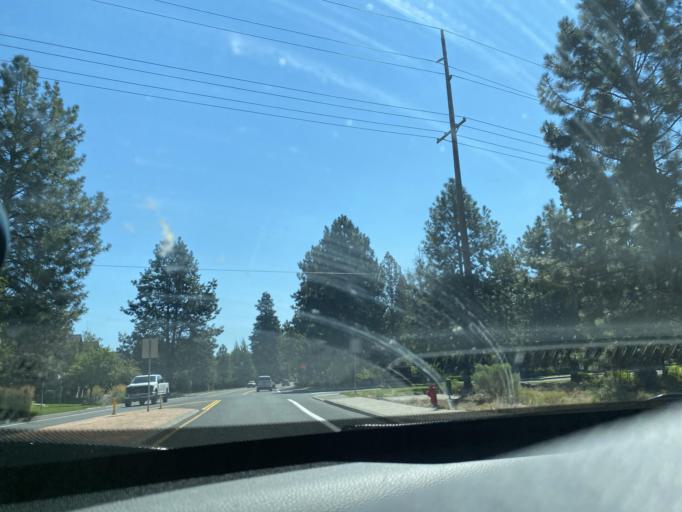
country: US
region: Oregon
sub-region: Deschutes County
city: Bend
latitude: 44.0639
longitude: -121.3437
